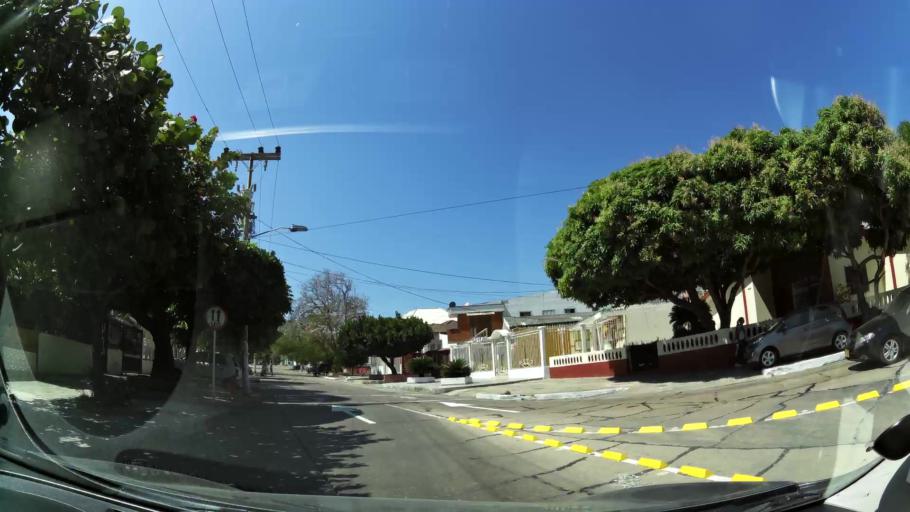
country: CO
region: Atlantico
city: Barranquilla
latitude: 11.0021
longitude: -74.7947
